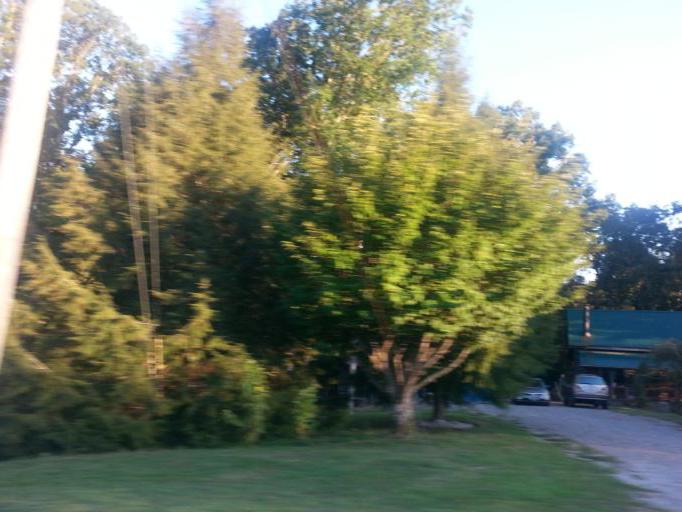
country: US
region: Tennessee
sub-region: Knox County
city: Knoxville
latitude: 35.9008
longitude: -83.8433
